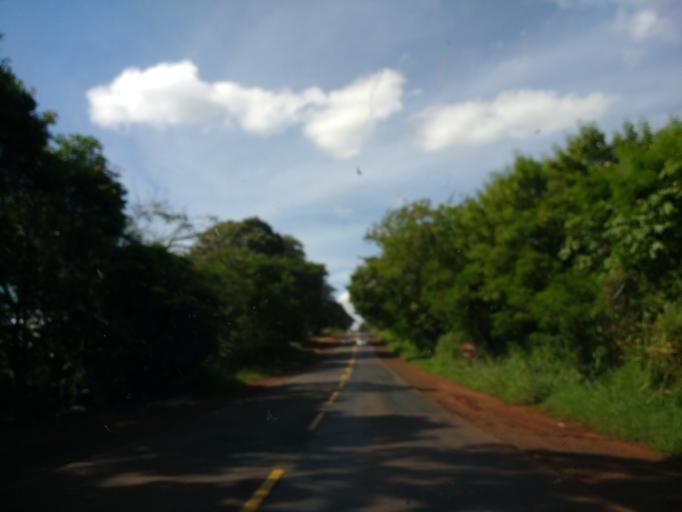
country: BR
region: Parana
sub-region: Engenheiro Beltrao
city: Engenheiro Beltrao
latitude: -23.5671
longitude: -52.2576
